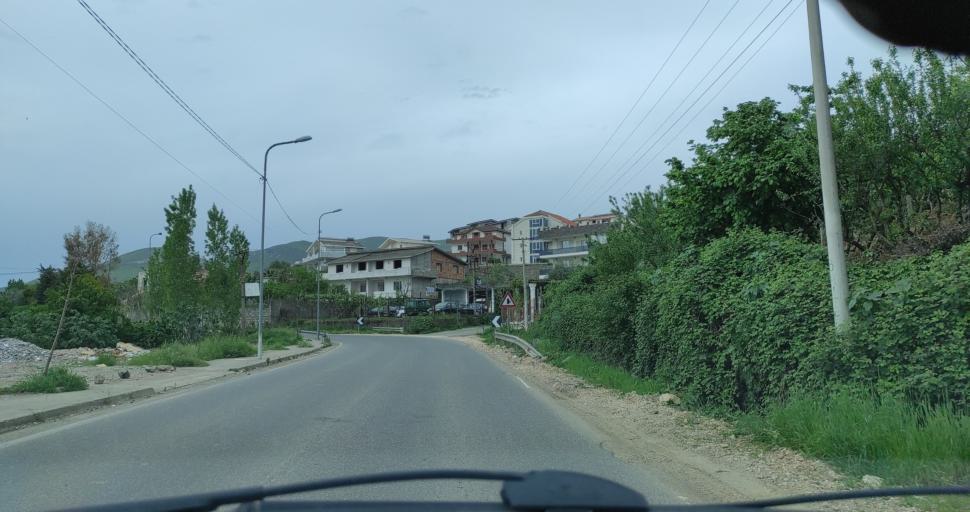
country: AL
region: Lezhe
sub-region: Rrethi i Kurbinit
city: Lac
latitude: 41.6261
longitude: 19.7098
